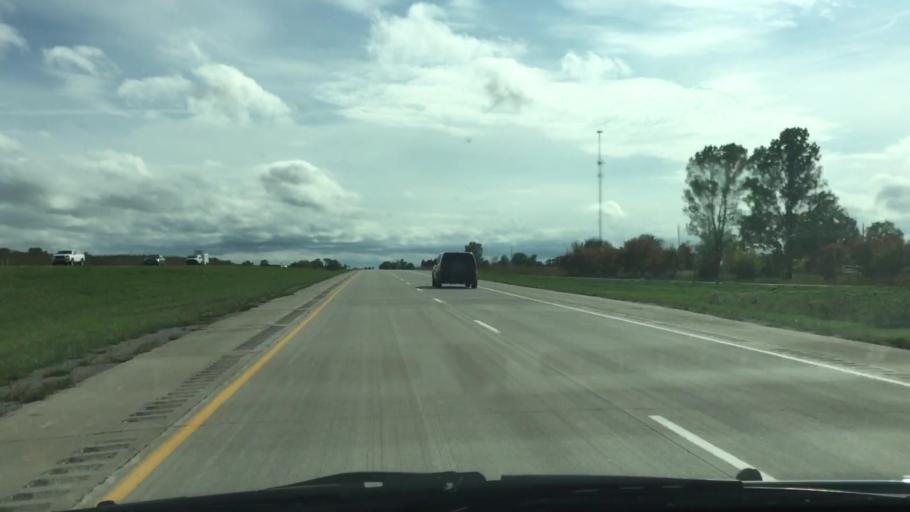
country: US
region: Iowa
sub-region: Decatur County
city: Leon
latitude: 40.8677
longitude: -93.8029
